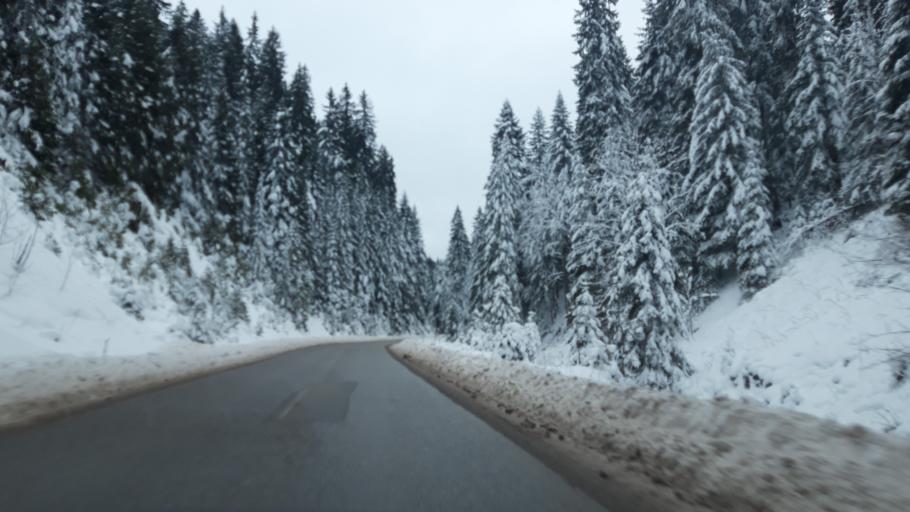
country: BA
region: Republika Srpska
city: Koran
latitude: 43.7650
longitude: 18.5466
